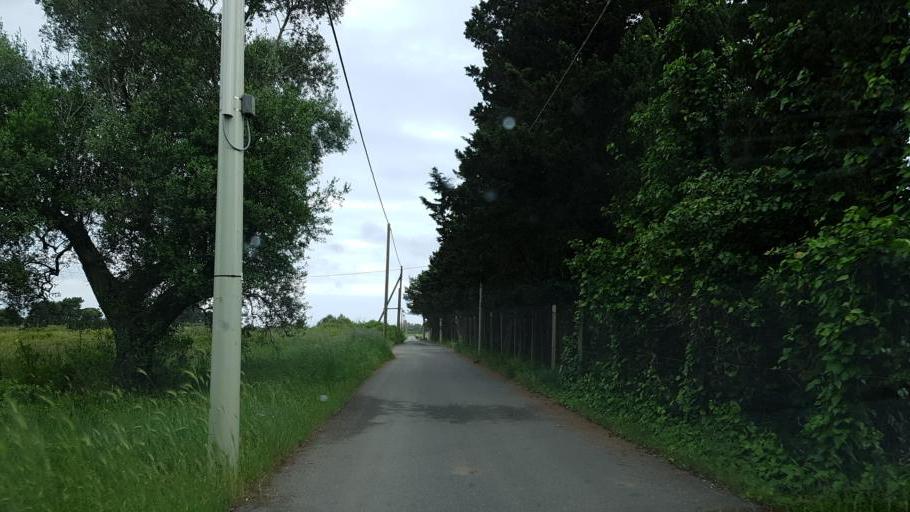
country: IT
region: Apulia
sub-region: Provincia di Brindisi
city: Brindisi
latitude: 40.6574
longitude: 17.9162
